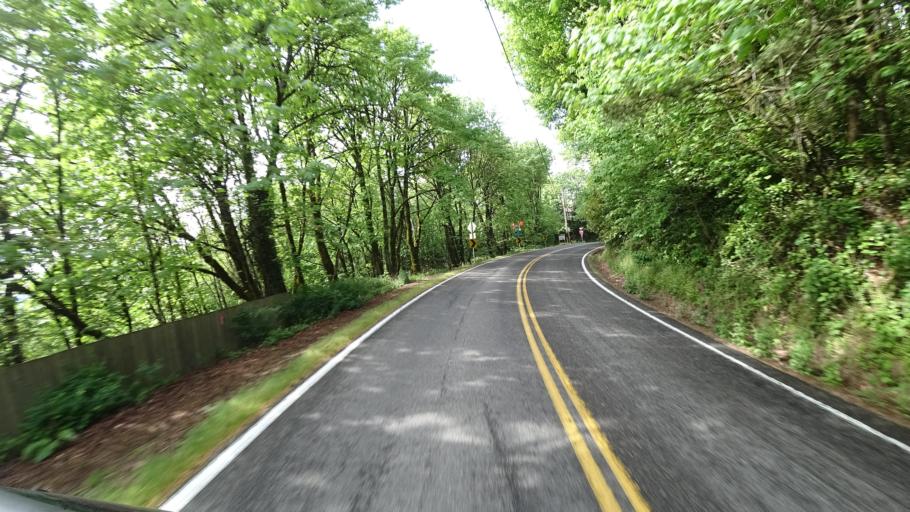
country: US
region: Oregon
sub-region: Washington County
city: West Haven
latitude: 45.5426
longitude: -122.7610
